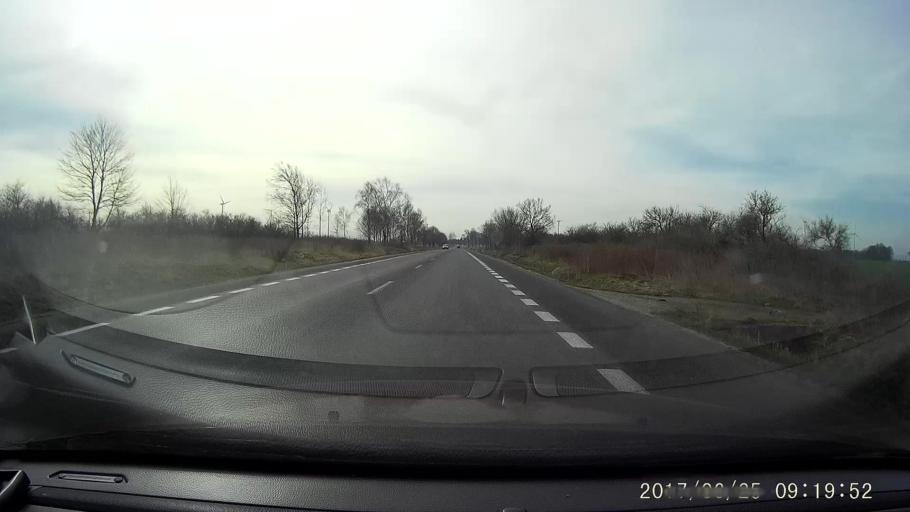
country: PL
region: Lower Silesian Voivodeship
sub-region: Powiat zgorzelecki
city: Zgorzelec
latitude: 51.1011
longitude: 15.0192
